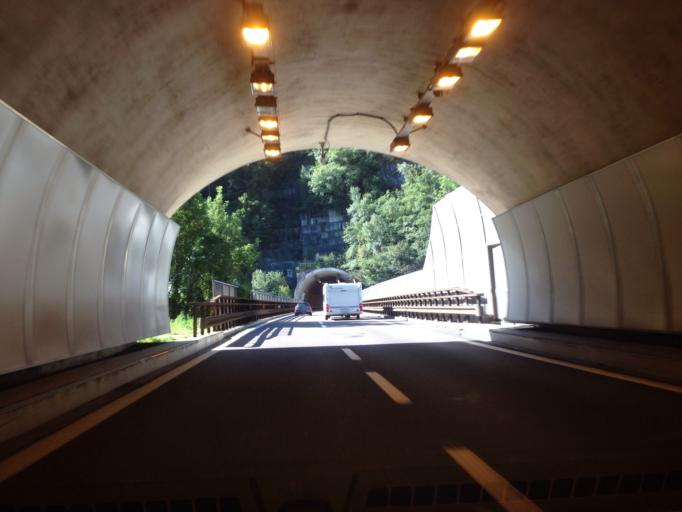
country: IT
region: Trentino-Alto Adige
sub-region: Bolzano
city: Ponte Gardena
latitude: 46.5989
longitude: 11.5335
